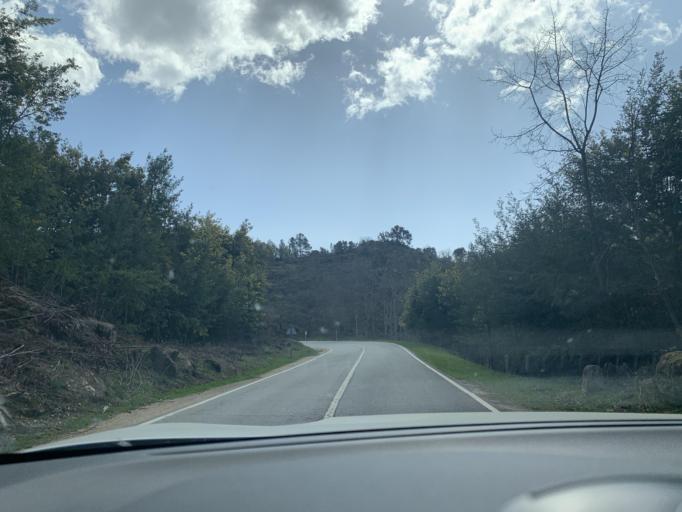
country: PT
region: Guarda
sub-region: Fornos de Algodres
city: Fornos de Algodres
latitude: 40.5693
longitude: -7.5937
